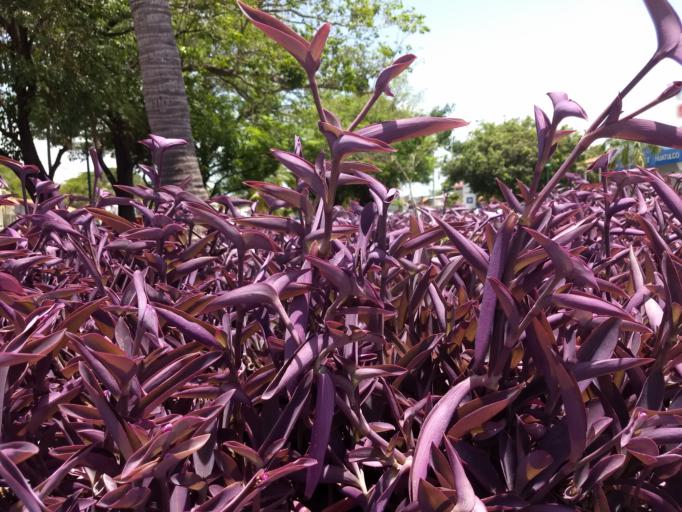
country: MX
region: Oaxaca
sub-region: Santa Maria Huatulco
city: Crucecita
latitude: 15.7639
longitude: -96.1328
